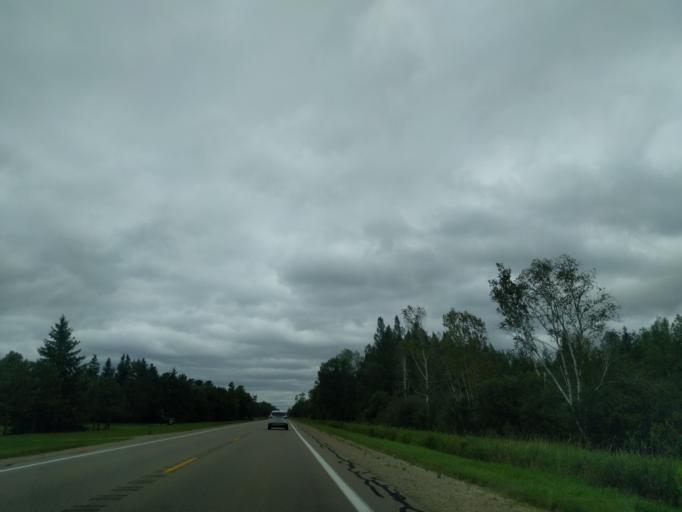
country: US
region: Michigan
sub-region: Delta County
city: Escanaba
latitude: 45.5003
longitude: -87.2921
